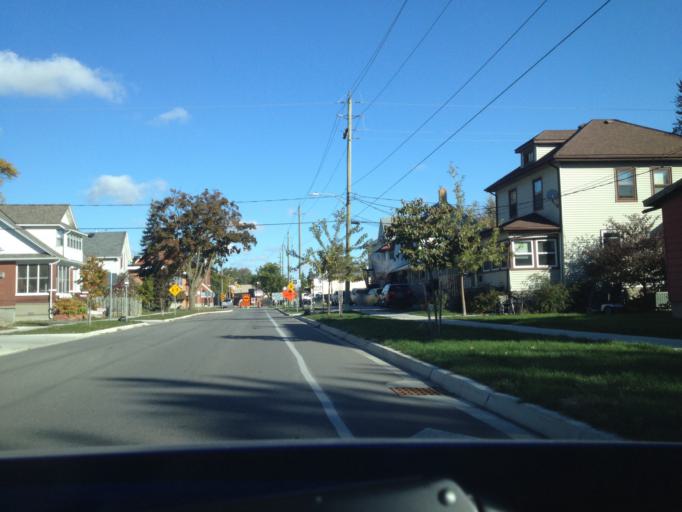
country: CA
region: Ontario
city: Amherstburg
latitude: 42.0505
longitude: -82.6024
